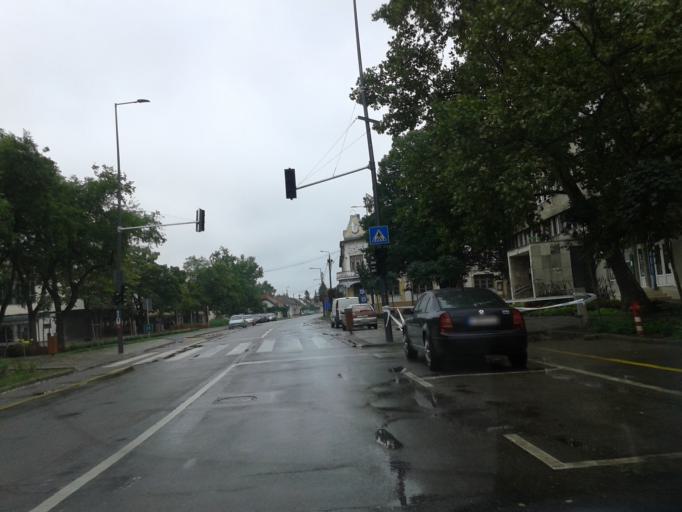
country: HU
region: Bacs-Kiskun
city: Kiskoros
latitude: 46.6201
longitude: 19.2842
